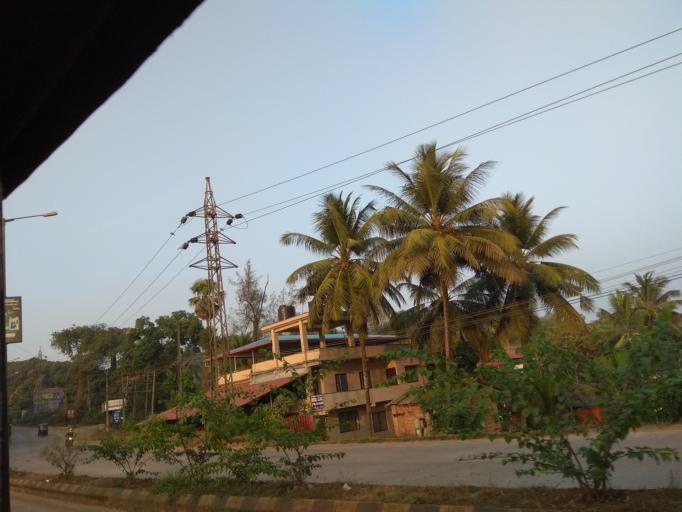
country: IN
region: Karnataka
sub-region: Dakshina Kannada
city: Mangalore
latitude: 12.9326
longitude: 74.8590
